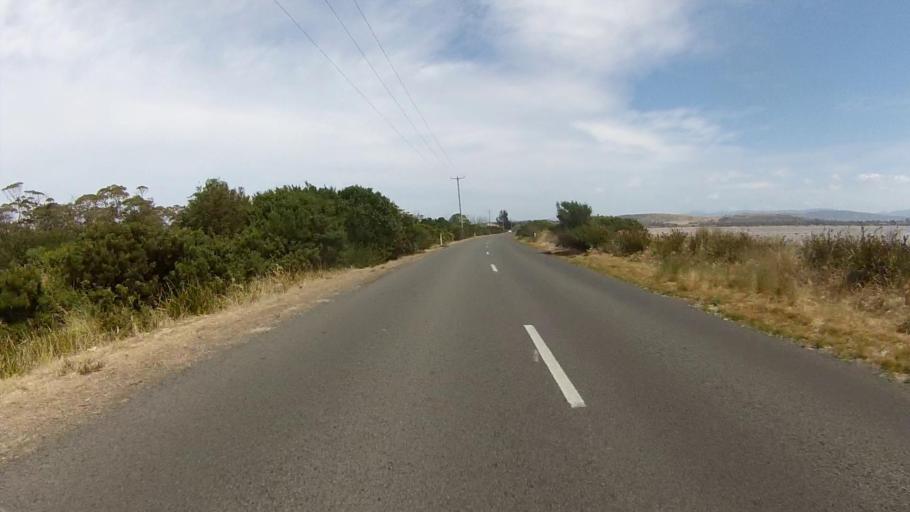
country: AU
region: Tasmania
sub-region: Clarence
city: Sandford
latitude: -43.0281
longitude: 147.4669
